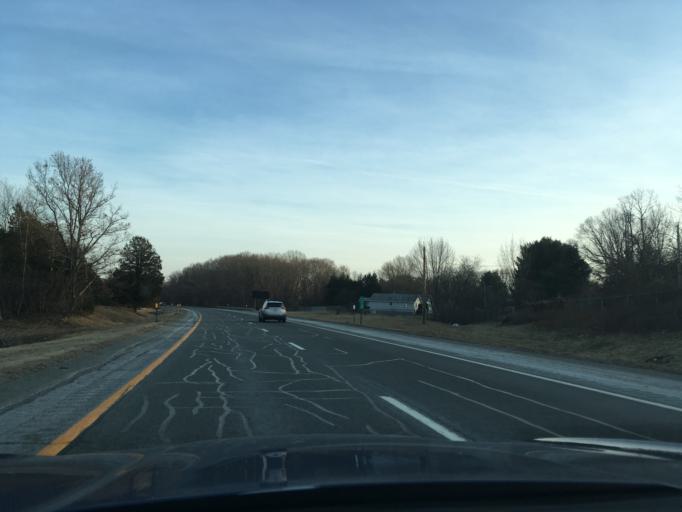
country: US
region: Rhode Island
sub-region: Providence County
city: Johnston
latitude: 41.7801
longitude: -71.5009
